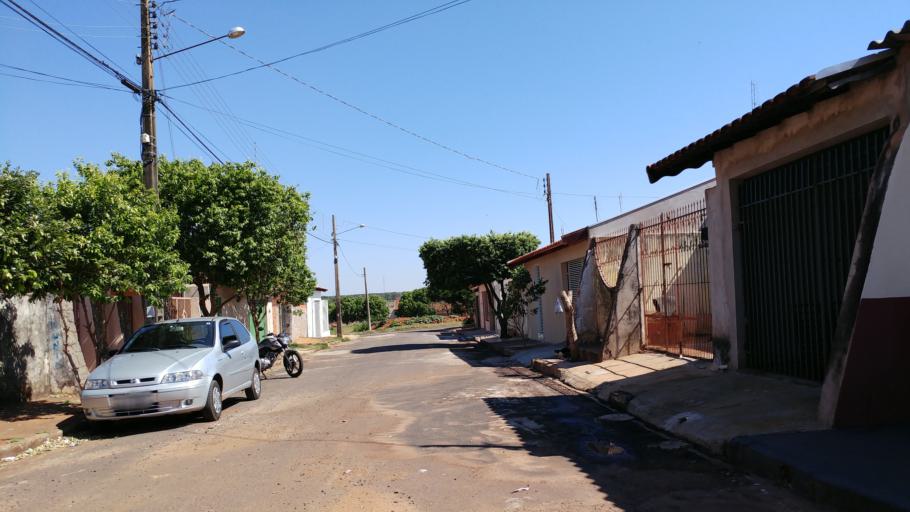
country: BR
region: Sao Paulo
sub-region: Paraguacu Paulista
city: Paraguacu Paulista
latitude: -22.4364
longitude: -50.5808
